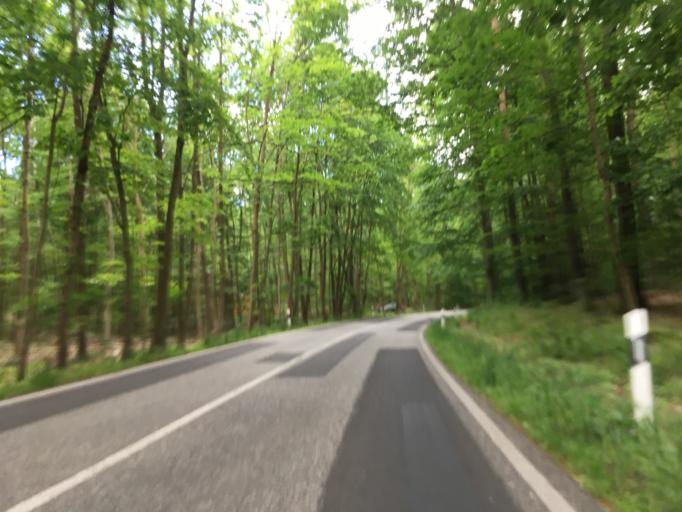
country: DE
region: Brandenburg
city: Bad Freienwalde
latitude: 52.7458
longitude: 13.9867
